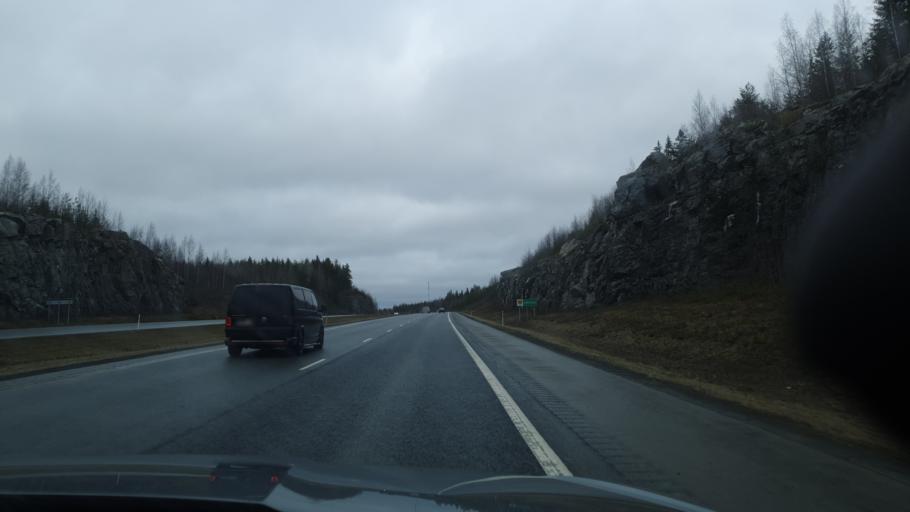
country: FI
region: Pirkanmaa
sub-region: Etelae-Pirkanmaa
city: Toijala
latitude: 61.2406
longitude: 23.8379
